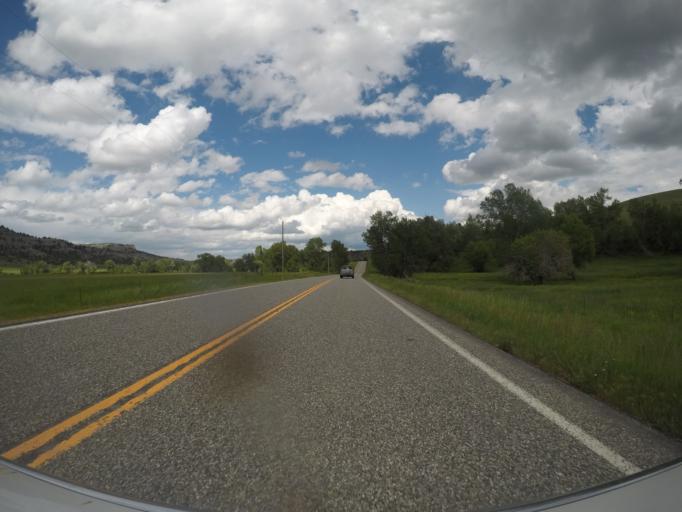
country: US
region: Montana
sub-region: Sweet Grass County
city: Big Timber
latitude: 45.6949
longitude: -110.0337
